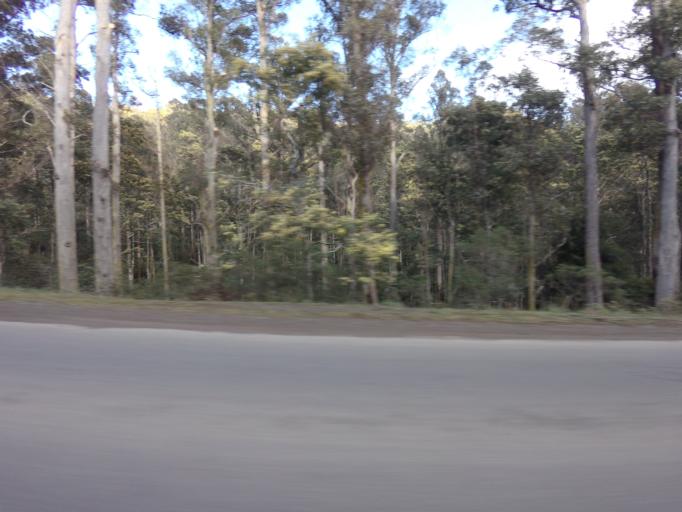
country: AU
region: Tasmania
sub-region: Huon Valley
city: Geeveston
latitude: -43.2308
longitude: 146.9884
